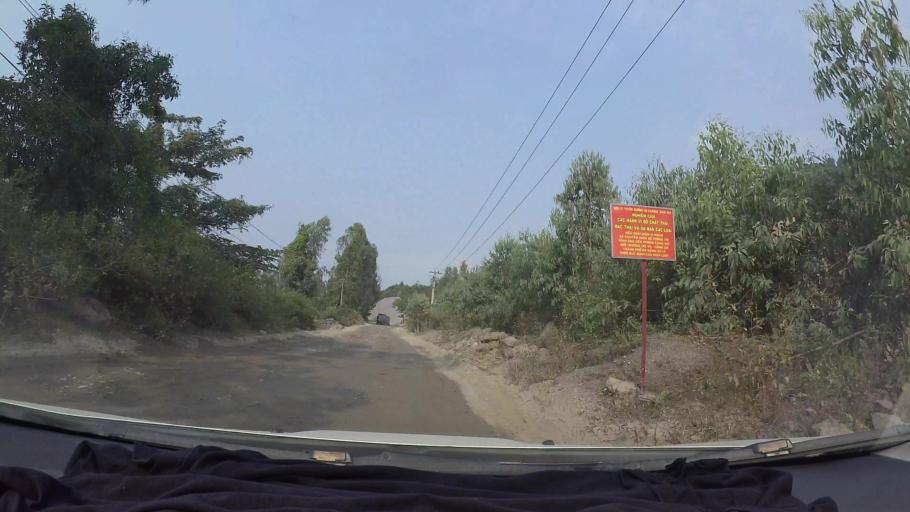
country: VN
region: Da Nang
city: Lien Chieu
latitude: 16.0393
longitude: 108.1580
